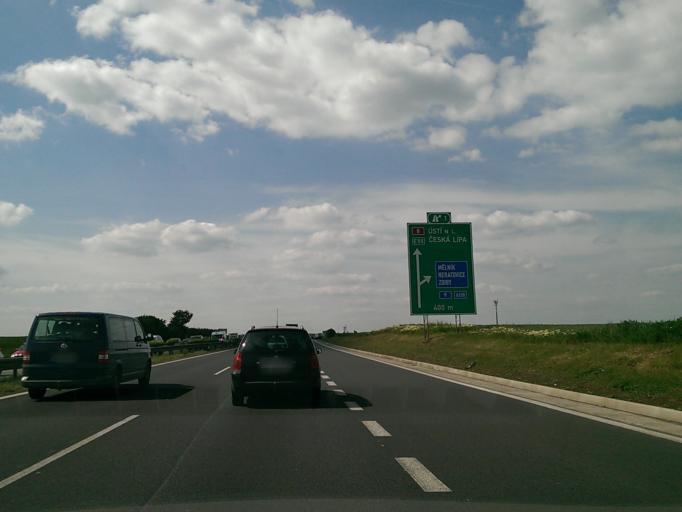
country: CZ
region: Central Bohemia
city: Zdiby
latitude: 50.1708
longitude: 14.4594
